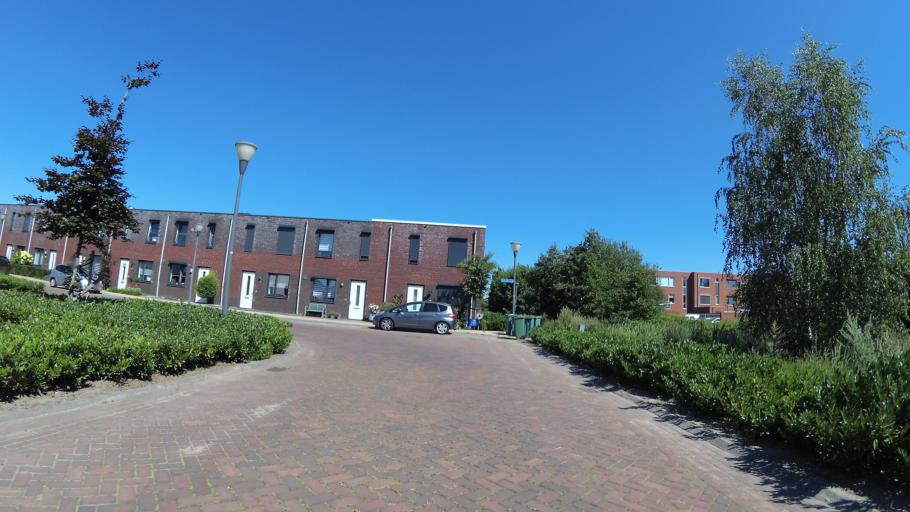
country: NL
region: North Brabant
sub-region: Gemeente Waalwijk
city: Waalwijk
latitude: 51.6738
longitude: 5.0420
